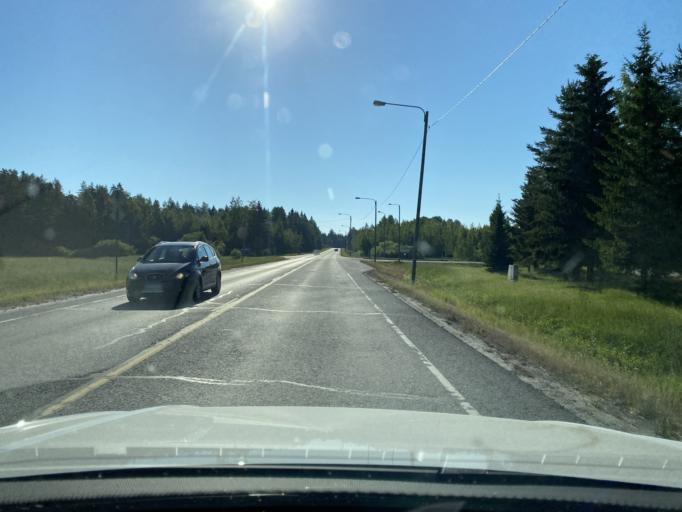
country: FI
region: Haeme
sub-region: Forssa
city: Tammela
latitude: 60.8304
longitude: 23.7144
